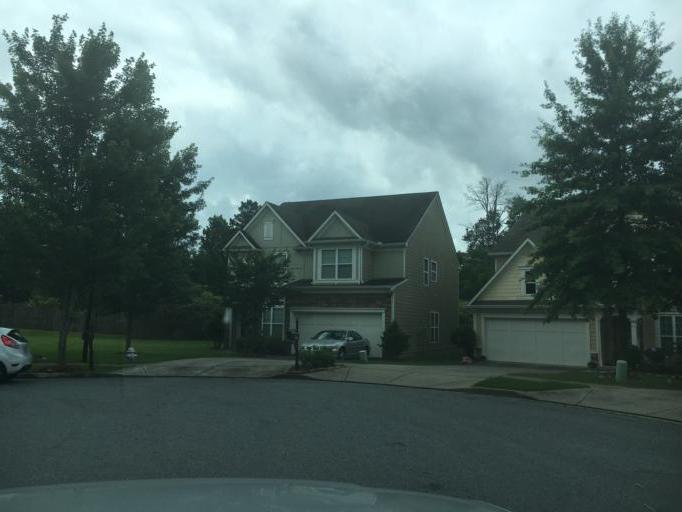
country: US
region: Georgia
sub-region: Gwinnett County
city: Duluth
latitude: 33.9768
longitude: -84.1072
